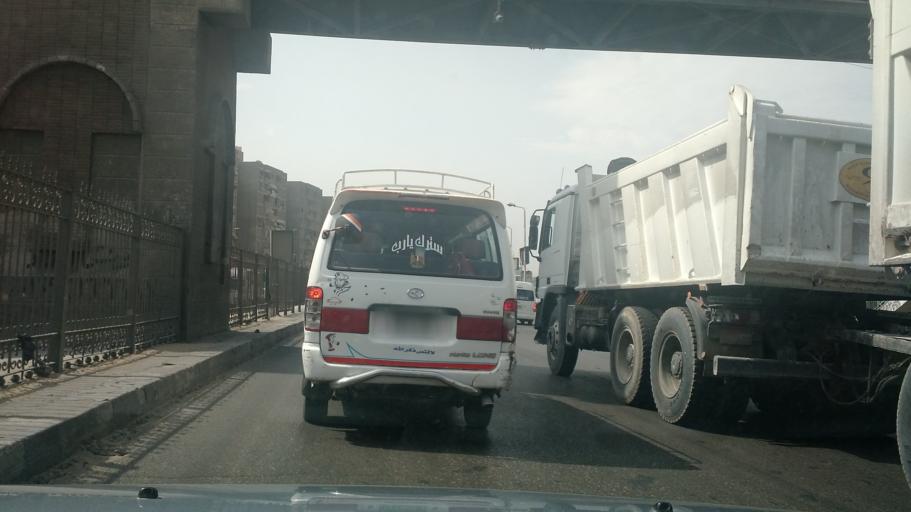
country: EG
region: Al Jizah
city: Al Jizah
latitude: 29.9866
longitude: 31.2886
